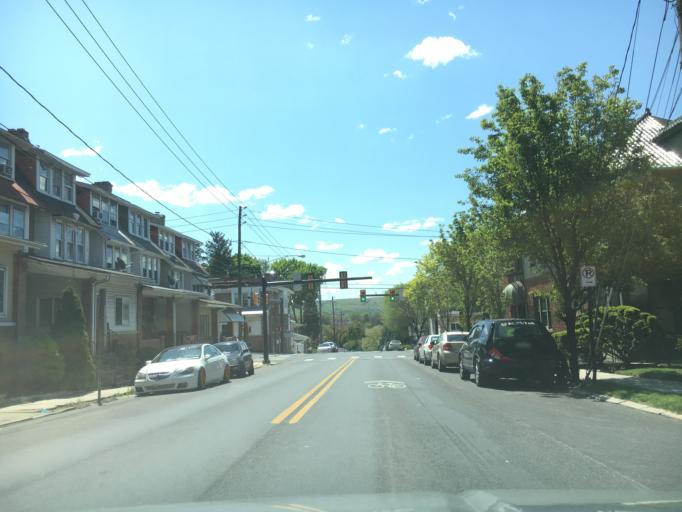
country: US
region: Pennsylvania
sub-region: Lehigh County
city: Allentown
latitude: 40.5957
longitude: -75.4871
